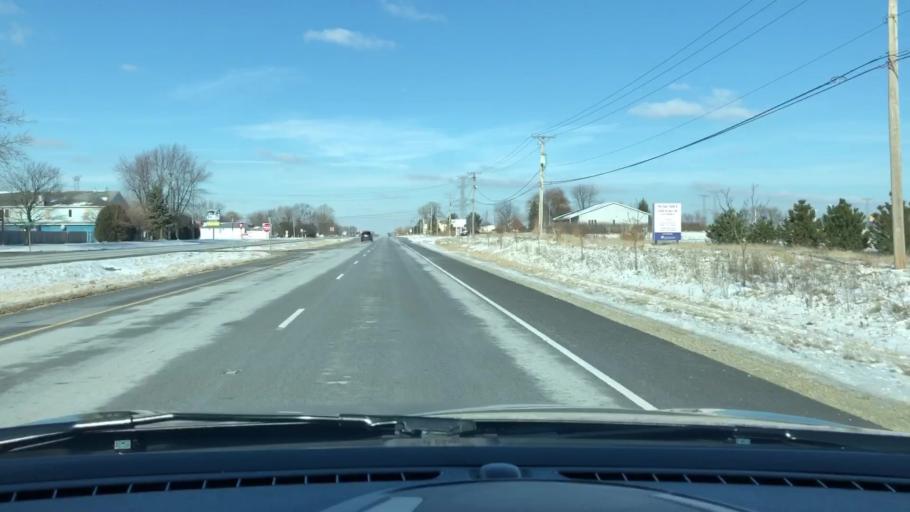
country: US
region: Illinois
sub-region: Will County
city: Preston Heights
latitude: 41.4488
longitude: -88.0790
